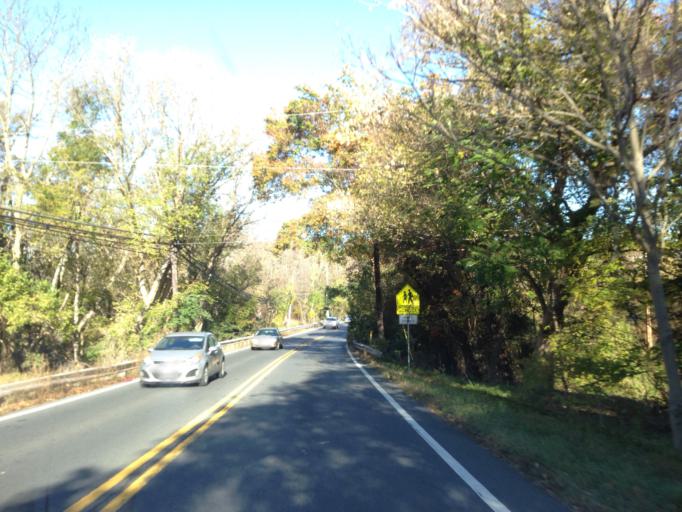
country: US
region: Maryland
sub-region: Montgomery County
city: Clarksburg
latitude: 39.2207
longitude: -77.2588
